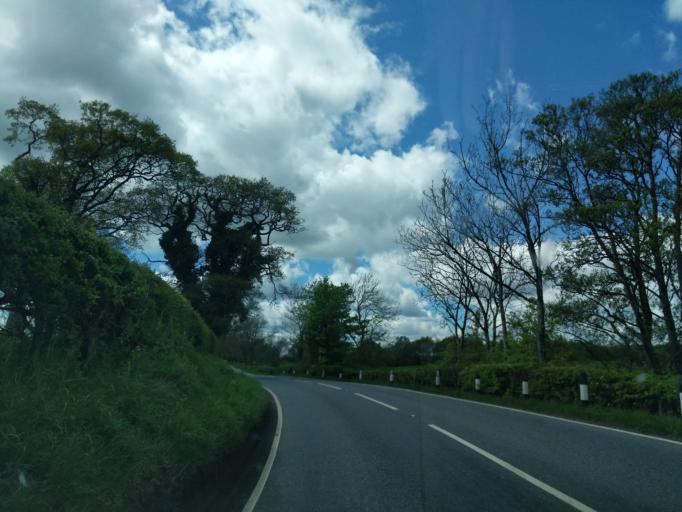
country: GB
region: Scotland
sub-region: Stirling
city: Doune
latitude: 56.1667
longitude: -4.0863
